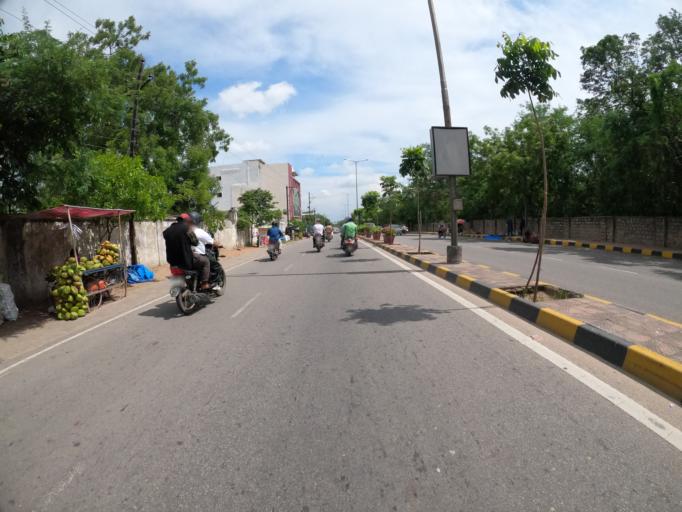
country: IN
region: Telangana
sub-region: Hyderabad
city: Hyderabad
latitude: 17.3904
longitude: 78.4230
